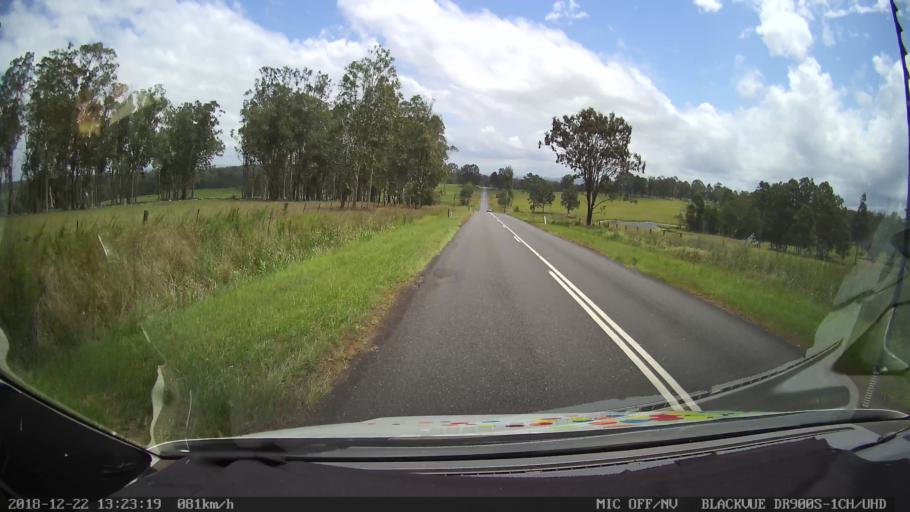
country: AU
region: New South Wales
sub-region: Clarence Valley
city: Coutts Crossing
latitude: -29.7965
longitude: 152.9080
